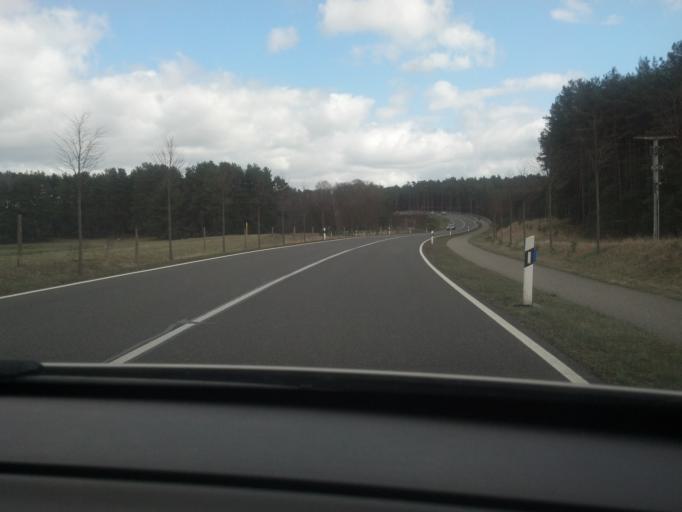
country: DE
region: Mecklenburg-Vorpommern
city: Neustrelitz
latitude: 53.3007
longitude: 13.0839
